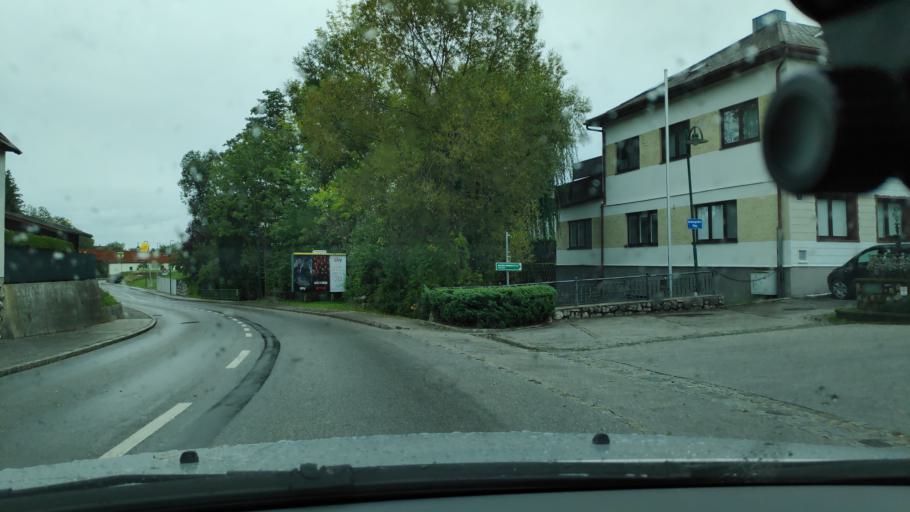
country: AT
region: Lower Austria
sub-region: Politischer Bezirk Neunkirchen
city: Willendorf am Steinfelde
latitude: 47.7909
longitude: 16.0465
